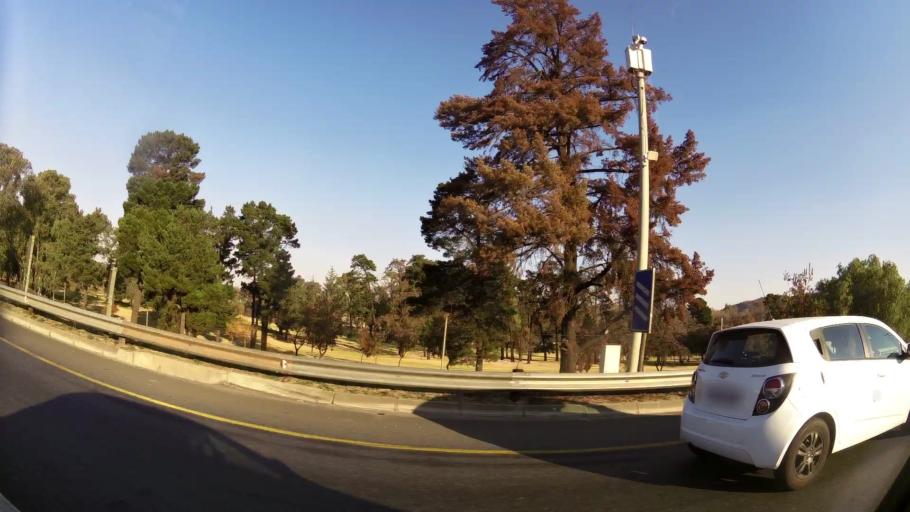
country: ZA
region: Gauteng
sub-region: Ekurhuleni Metropolitan Municipality
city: Germiston
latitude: -26.2612
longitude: 28.1063
